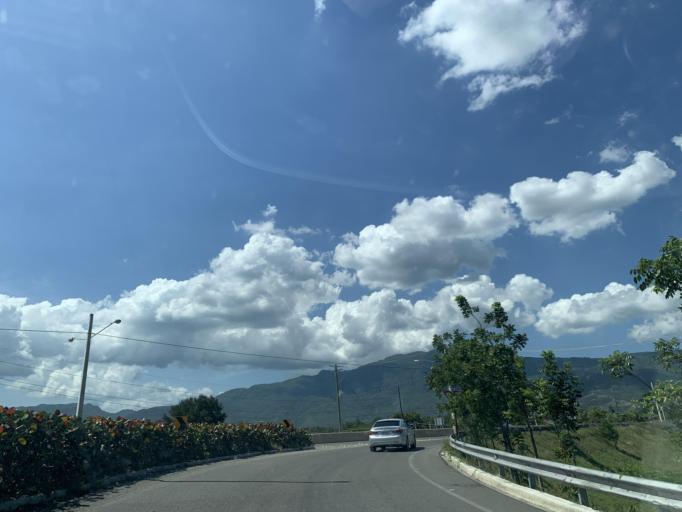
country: DO
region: Santiago
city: Villa Gonzalez
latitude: 19.5164
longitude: -70.7640
